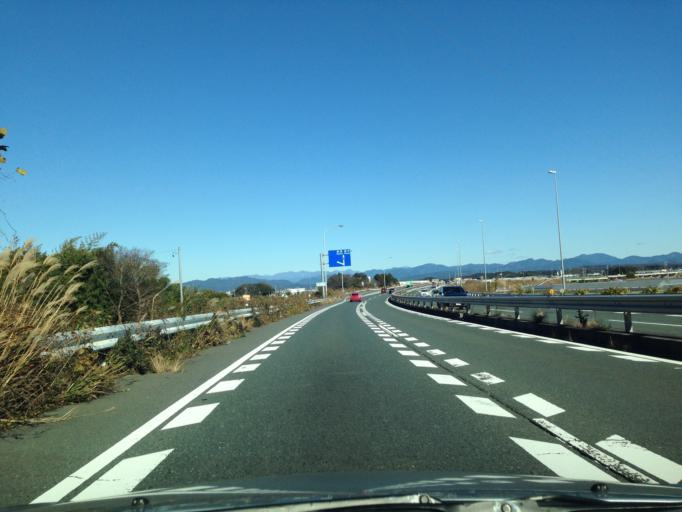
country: JP
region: Shizuoka
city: Fukuroi
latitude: 34.7434
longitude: 137.8918
